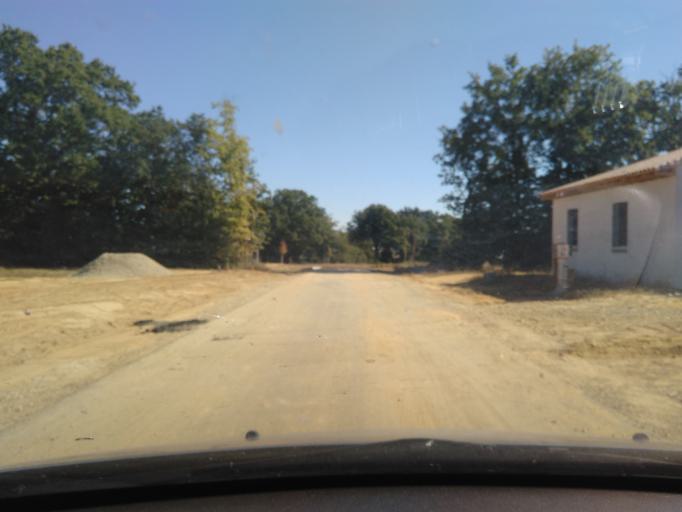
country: FR
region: Pays de la Loire
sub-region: Departement de la Vendee
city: Mouilleron-le-Captif
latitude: 46.7164
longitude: -1.4639
